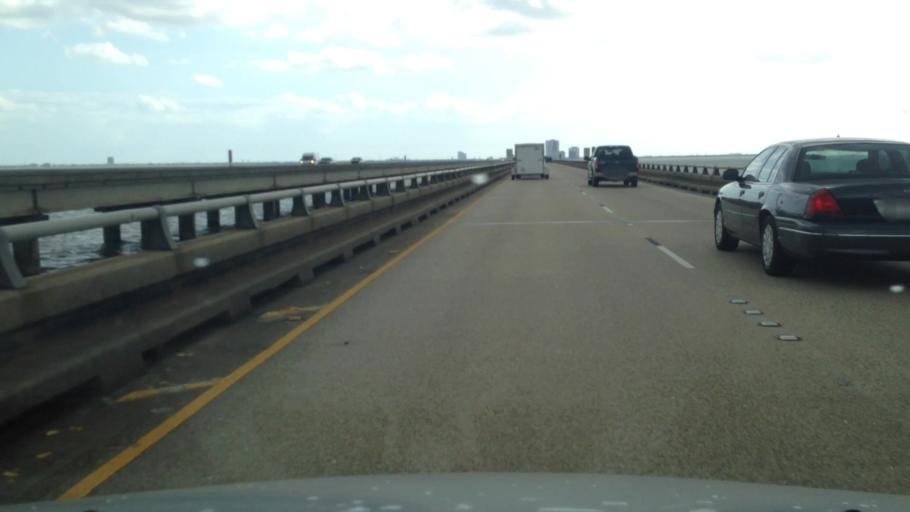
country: US
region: Louisiana
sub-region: Jefferson Parish
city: Metairie
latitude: 30.0701
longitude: -90.1456
